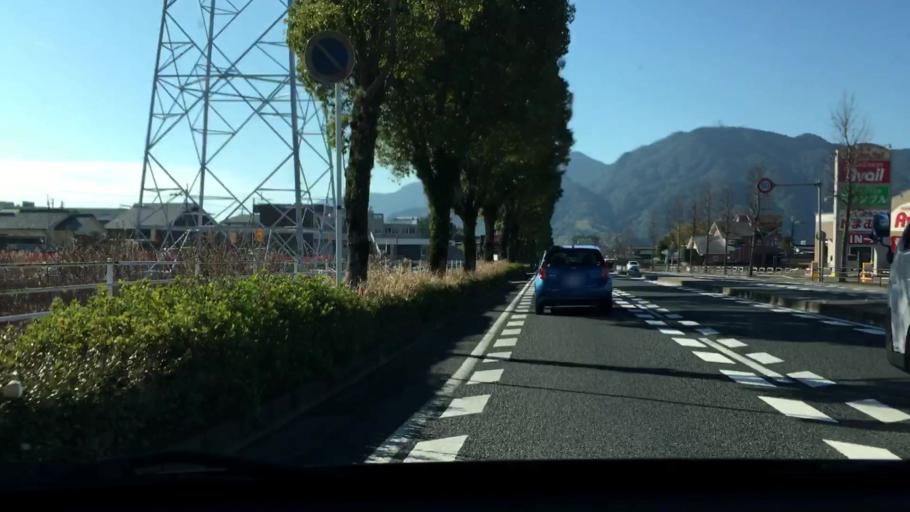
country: JP
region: Kagoshima
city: Kajiki
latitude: 31.7214
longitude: 130.6218
